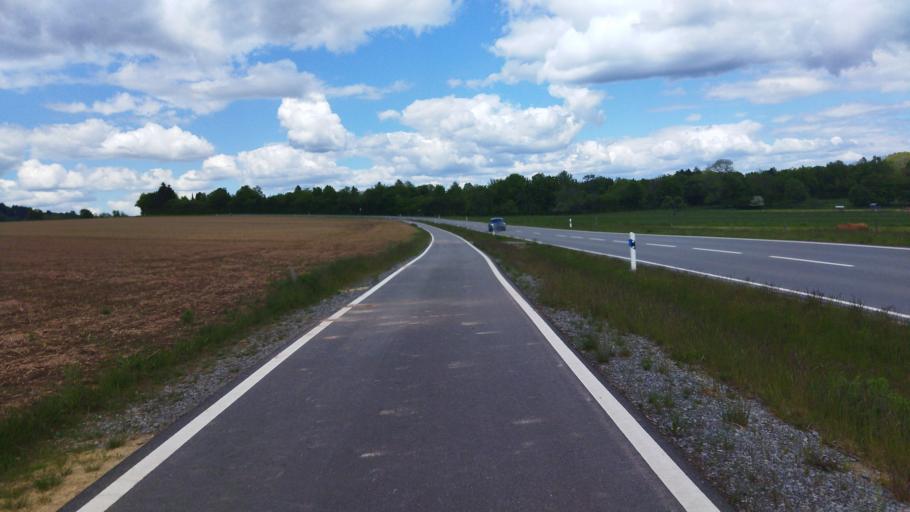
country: DE
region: Baden-Wuerttemberg
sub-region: Karlsruhe Region
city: Zwingenberg
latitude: 49.4531
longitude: 9.0552
